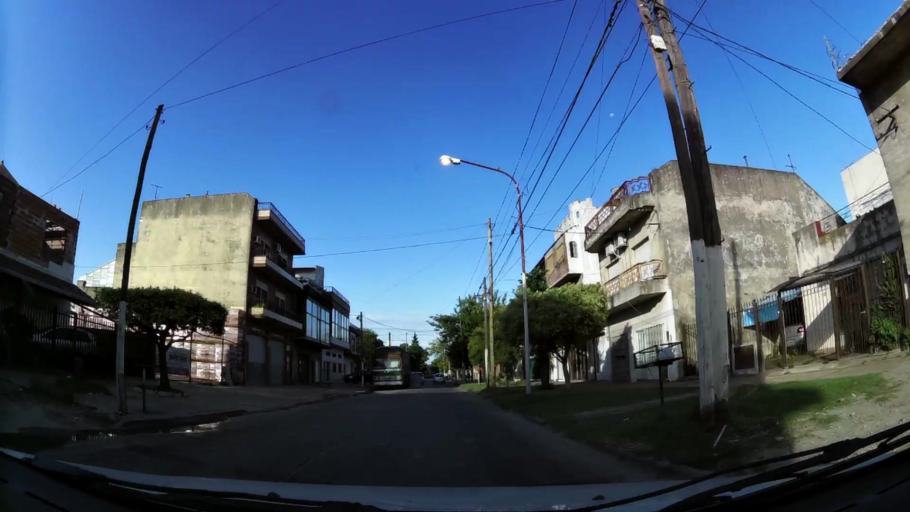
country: AR
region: Buenos Aires
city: Caseros
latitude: -34.5800
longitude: -58.5793
